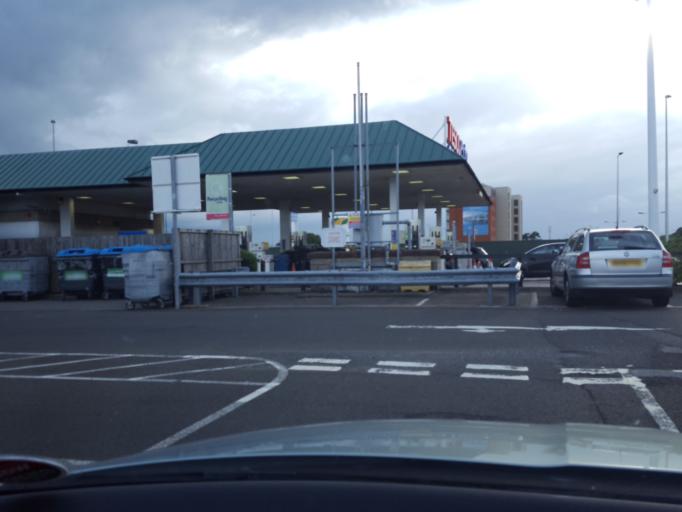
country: GB
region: Scotland
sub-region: Dundee City
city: Dundee
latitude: 56.4539
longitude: -2.9787
